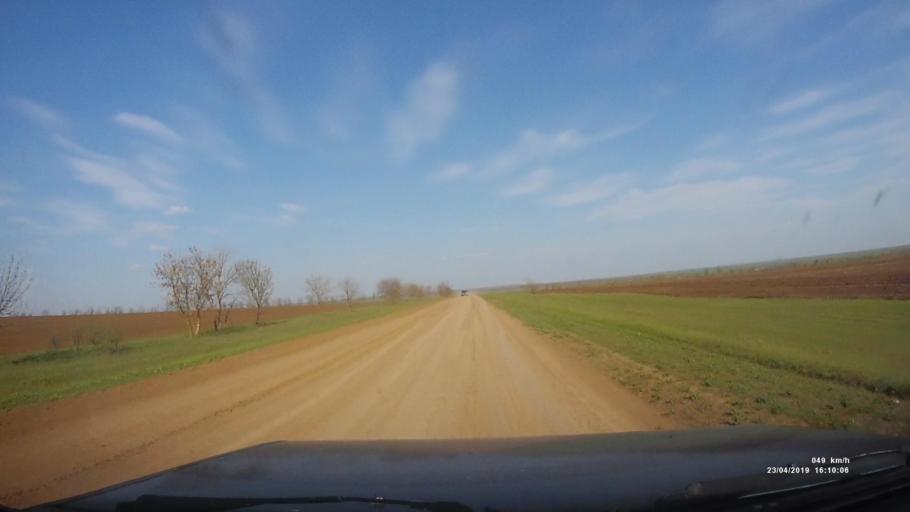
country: RU
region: Rostov
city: Remontnoye
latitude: 46.4820
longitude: 43.1187
